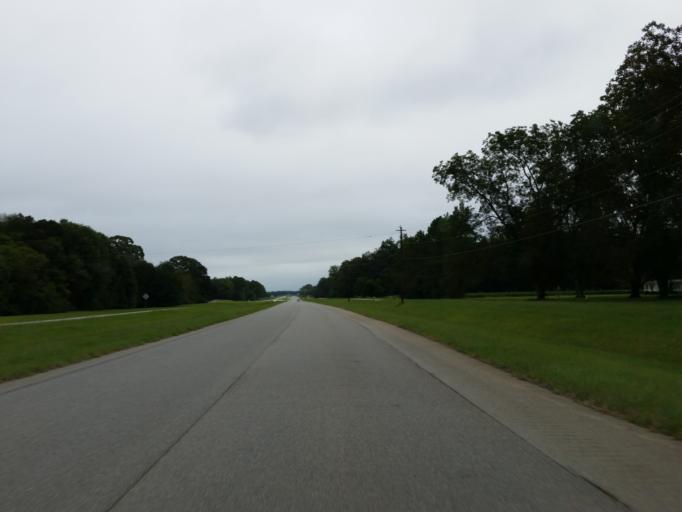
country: US
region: Georgia
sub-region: Houston County
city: Perry
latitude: 32.4302
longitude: -83.7489
